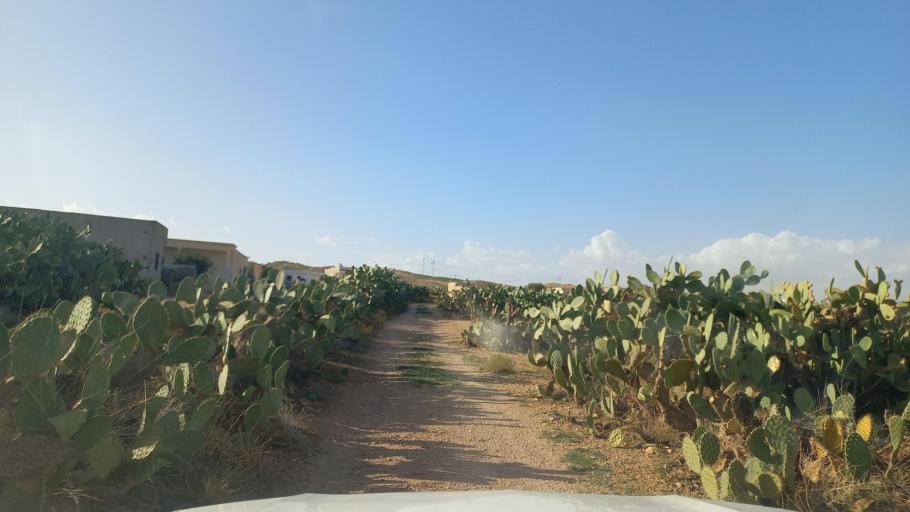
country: TN
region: Al Qasrayn
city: Sbiba
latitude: 35.3653
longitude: 9.0047
